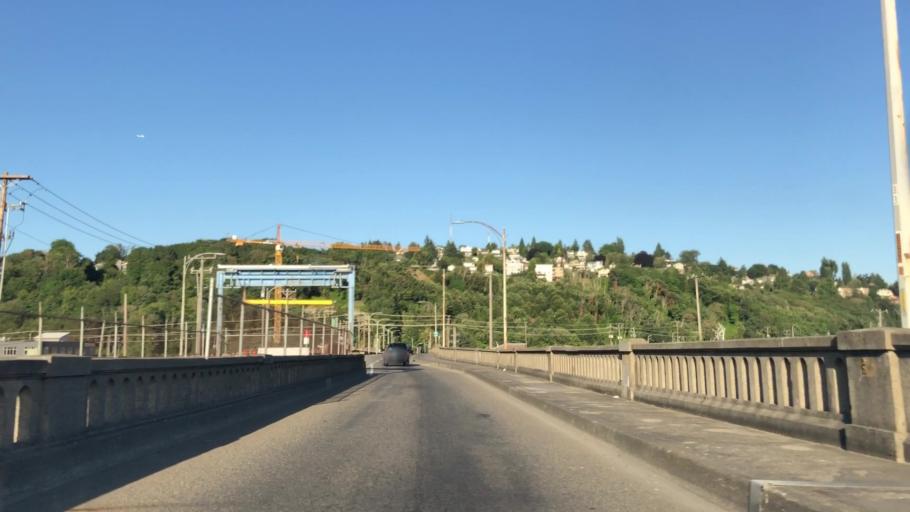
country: US
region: Washington
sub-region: King County
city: Seattle
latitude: 47.6334
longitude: -122.3805
